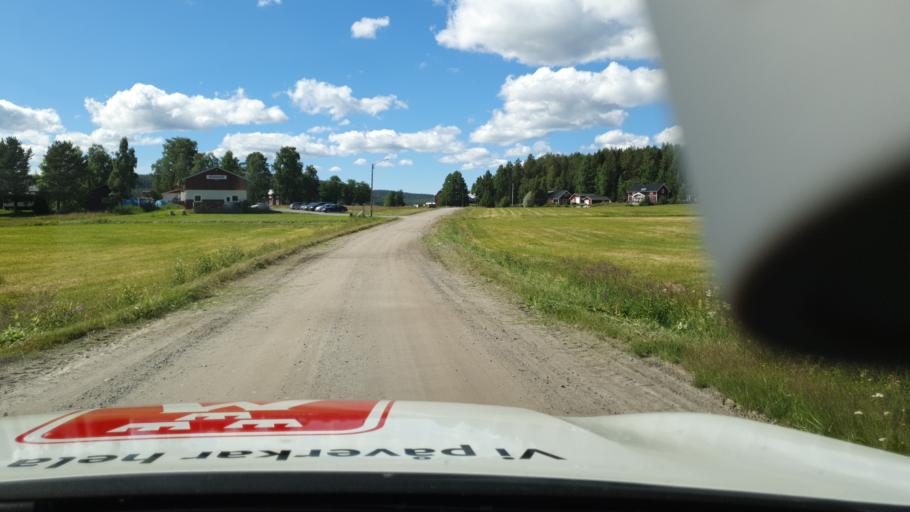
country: SE
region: Vaesterbotten
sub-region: Umea Kommun
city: Roback
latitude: 64.0045
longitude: 20.0761
